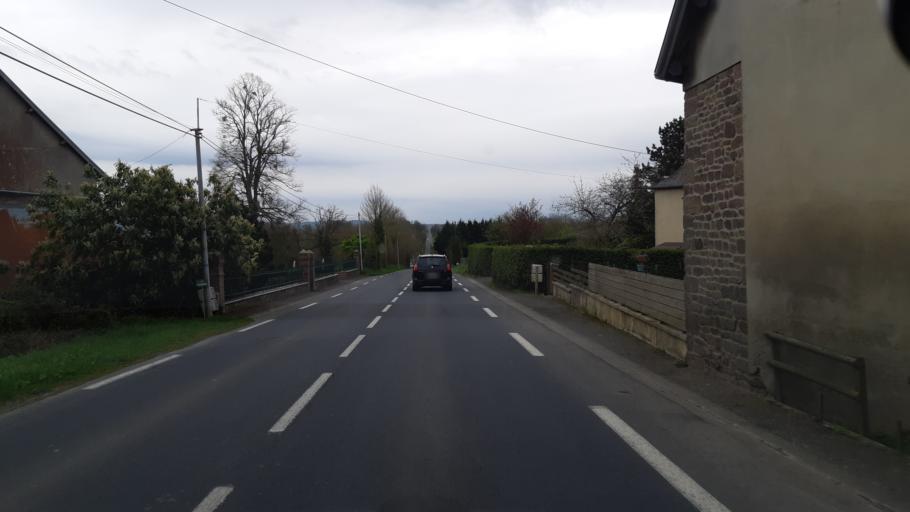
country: FR
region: Lower Normandy
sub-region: Departement de la Manche
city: Tessy-sur-Vire
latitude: 49.0254
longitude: -1.1454
